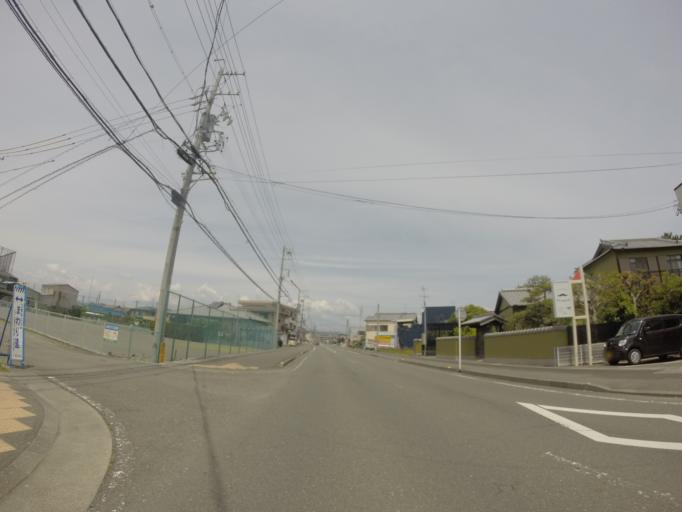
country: JP
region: Shizuoka
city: Fujieda
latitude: 34.8483
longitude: 138.2903
